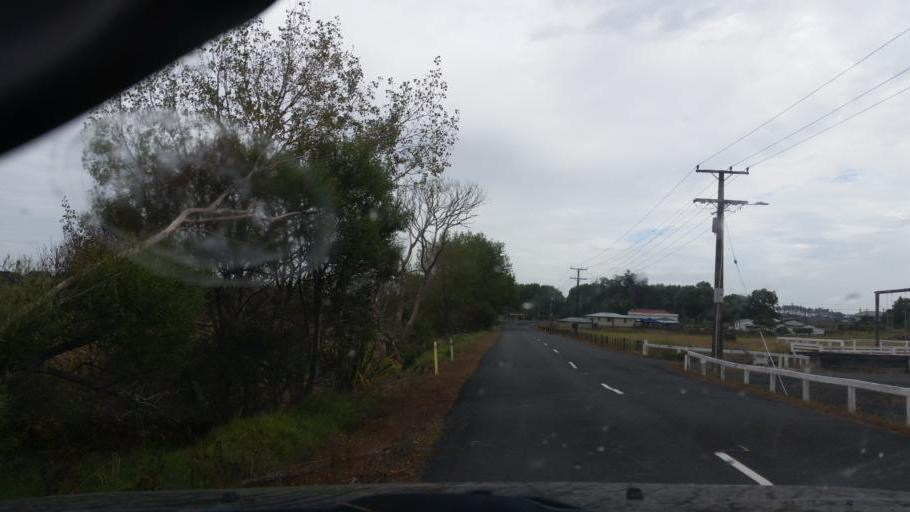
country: NZ
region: Northland
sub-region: Whangarei
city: Maungatapere
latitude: -35.8236
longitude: 174.0454
